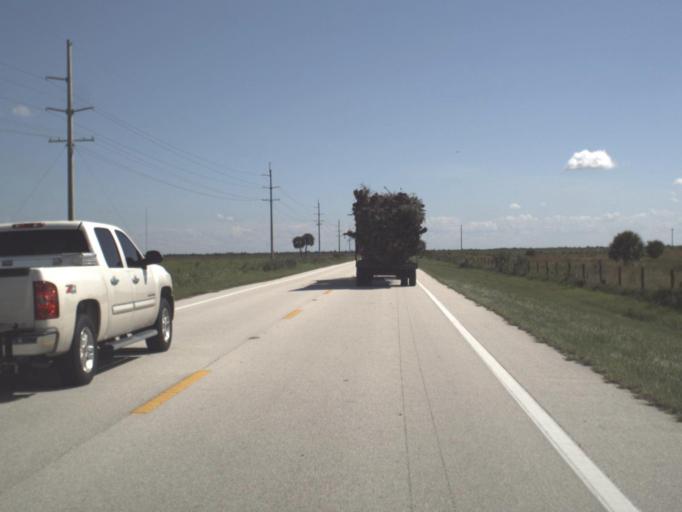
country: US
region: Florida
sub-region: Glades County
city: Moore Haven
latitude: 26.8123
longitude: -81.2422
